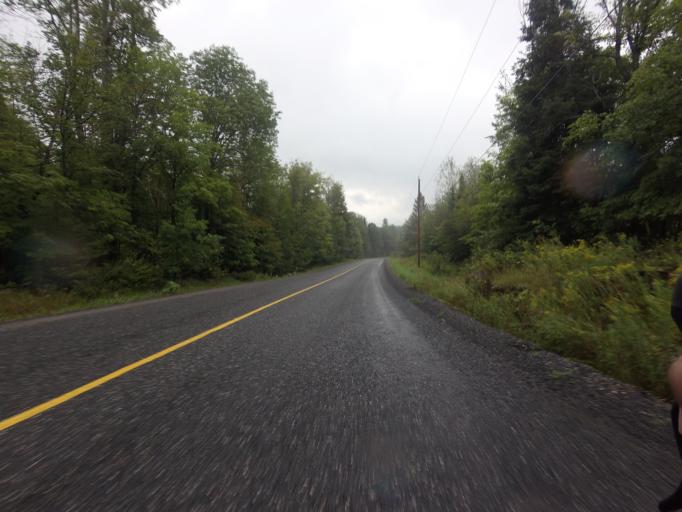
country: CA
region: Ontario
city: Perth
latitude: 45.0622
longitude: -76.5310
